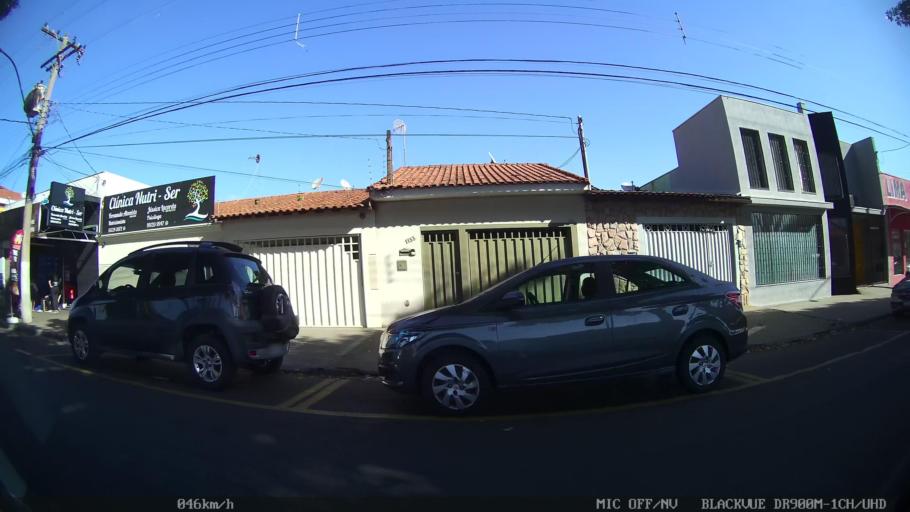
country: BR
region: Sao Paulo
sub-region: Franca
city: Franca
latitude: -20.4885
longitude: -47.4126
